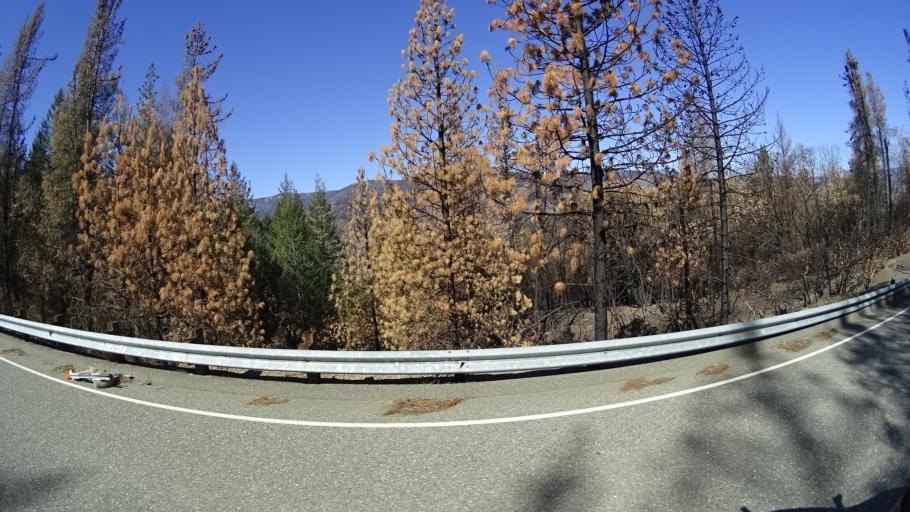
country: US
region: California
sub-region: Tehama County
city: Rancho Tehama Reserve
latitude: 39.6718
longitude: -122.7121
